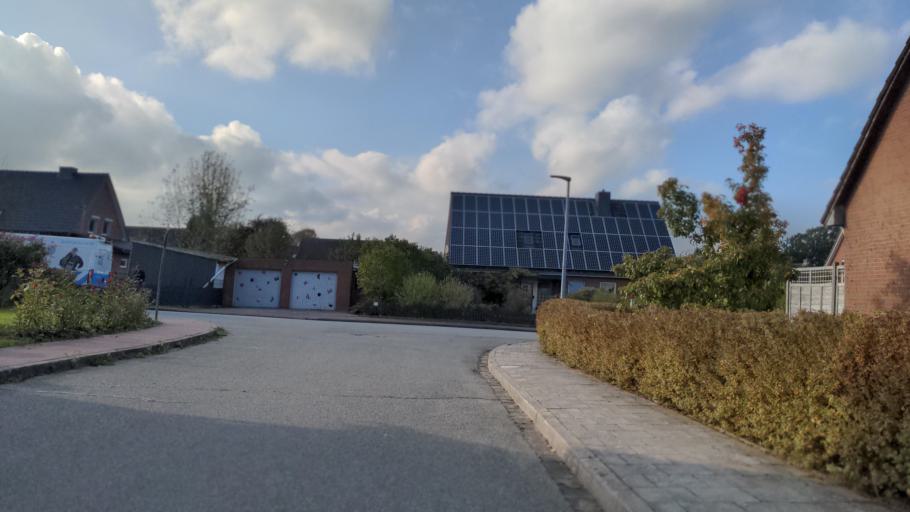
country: DE
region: Schleswig-Holstein
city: Beschendorf
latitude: 54.2082
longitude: 10.8736
